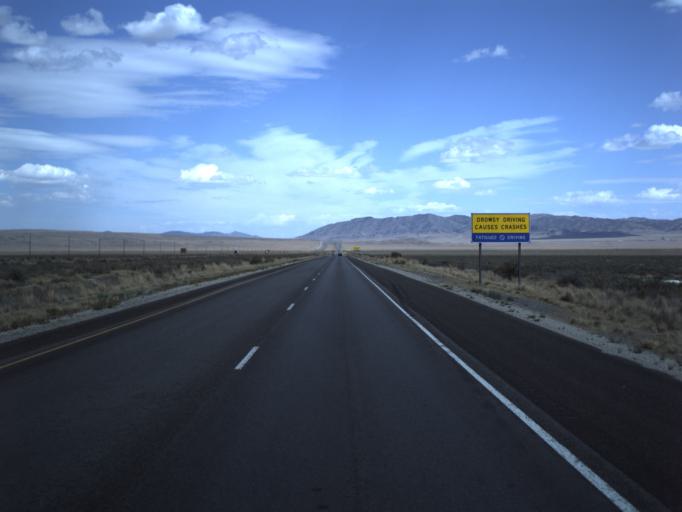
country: US
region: Utah
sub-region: Tooele County
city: Grantsville
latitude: 40.7336
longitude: -113.1062
